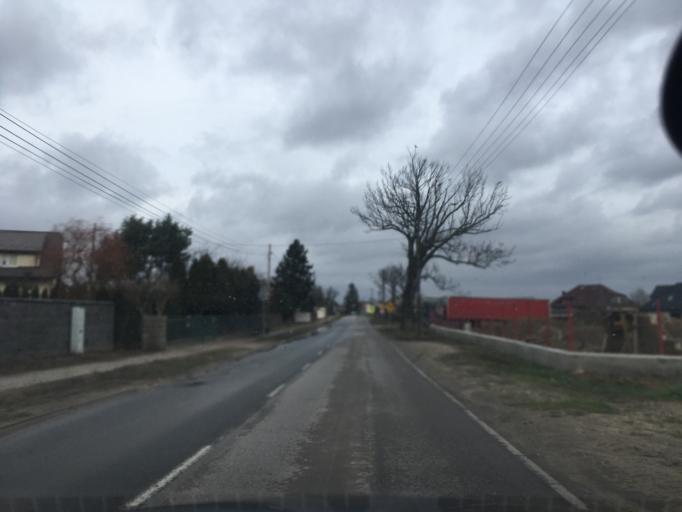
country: PL
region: Masovian Voivodeship
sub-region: Powiat piaseczynski
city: Lesznowola
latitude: 52.1062
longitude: 20.9317
